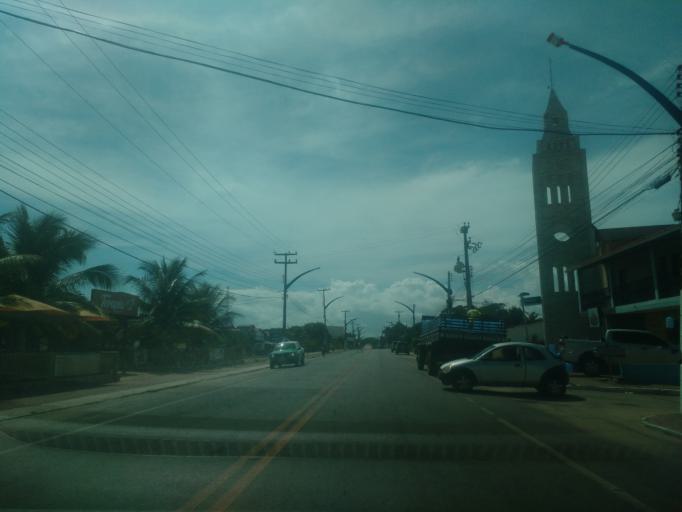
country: BR
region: Alagoas
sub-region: Marechal Deodoro
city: Marechal Deodoro
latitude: -9.7675
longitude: -35.8498
